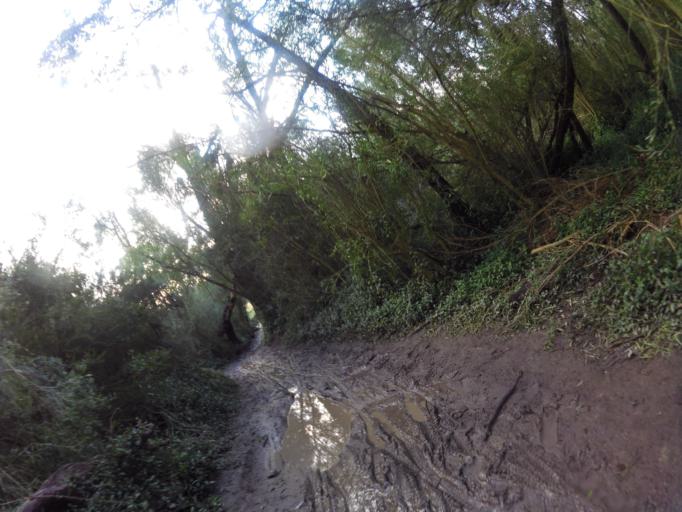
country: AU
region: Victoria
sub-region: Banyule
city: Viewbank
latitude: -37.7536
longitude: 145.0901
